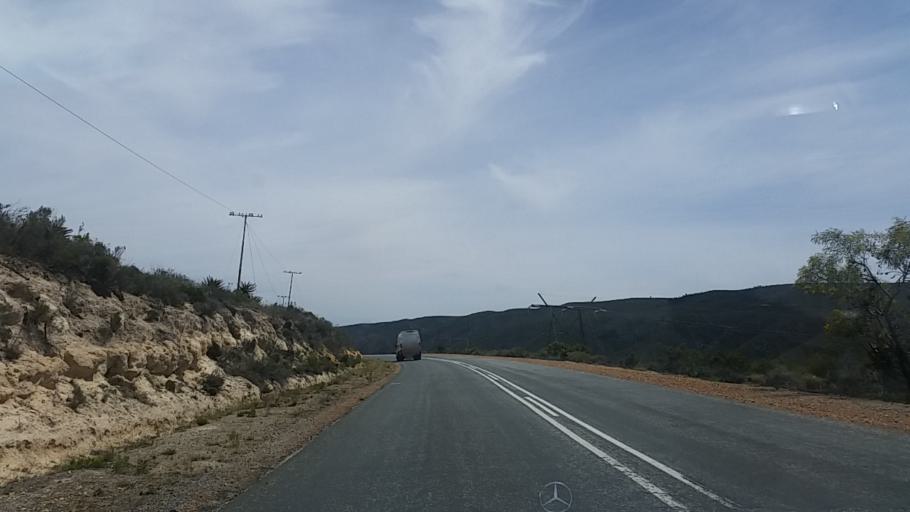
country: ZA
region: Western Cape
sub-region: Eden District Municipality
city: Knysna
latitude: -33.7420
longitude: 23.0263
